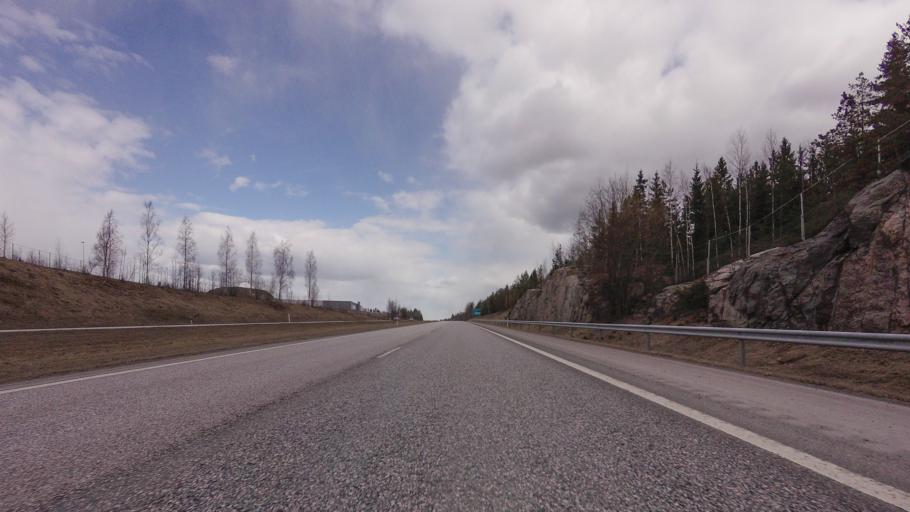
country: FI
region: Uusimaa
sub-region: Helsinki
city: Nurmijaervi
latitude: 60.4444
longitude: 24.8401
